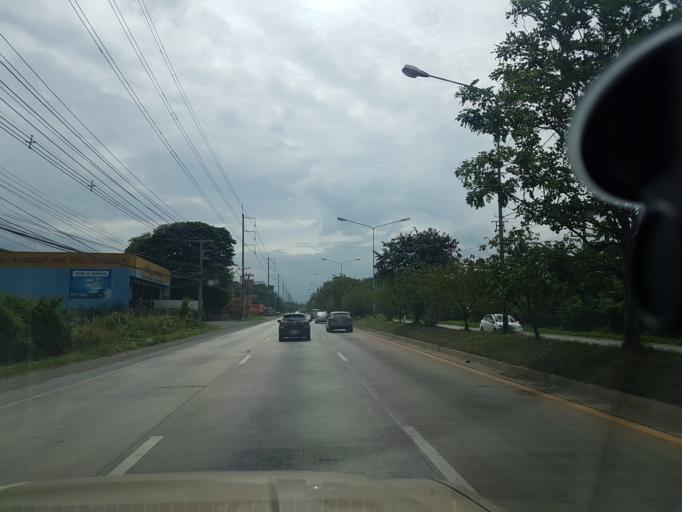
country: TH
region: Sara Buri
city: Phra Phutthabat
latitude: 14.7135
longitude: 100.8234
